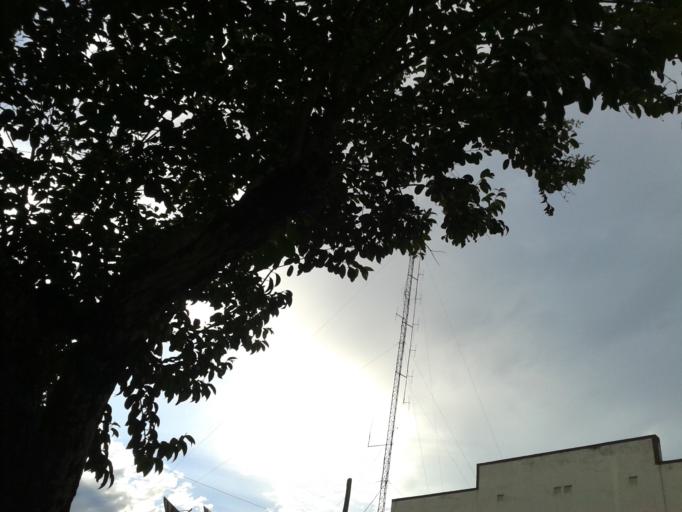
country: AR
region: Misiones
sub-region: Departamento de Obera
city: Obera
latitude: -27.4846
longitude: -55.1224
